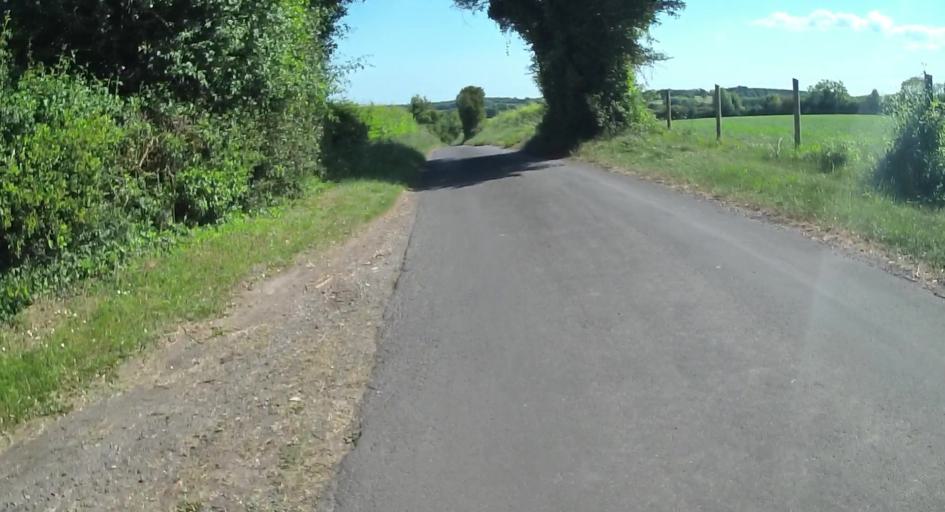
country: GB
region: England
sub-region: Hampshire
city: Old Basing
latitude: 51.2228
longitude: -1.0244
